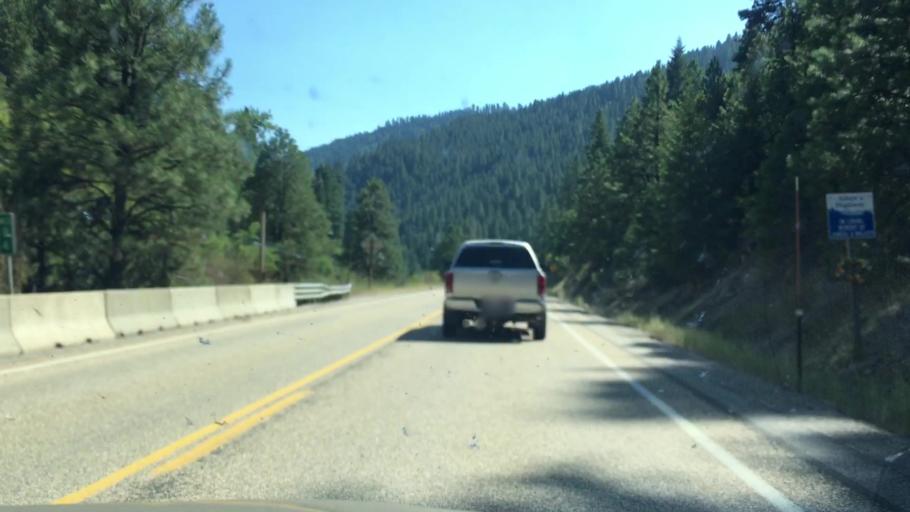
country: US
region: Idaho
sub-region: Valley County
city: Cascade
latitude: 44.1426
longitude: -116.1147
